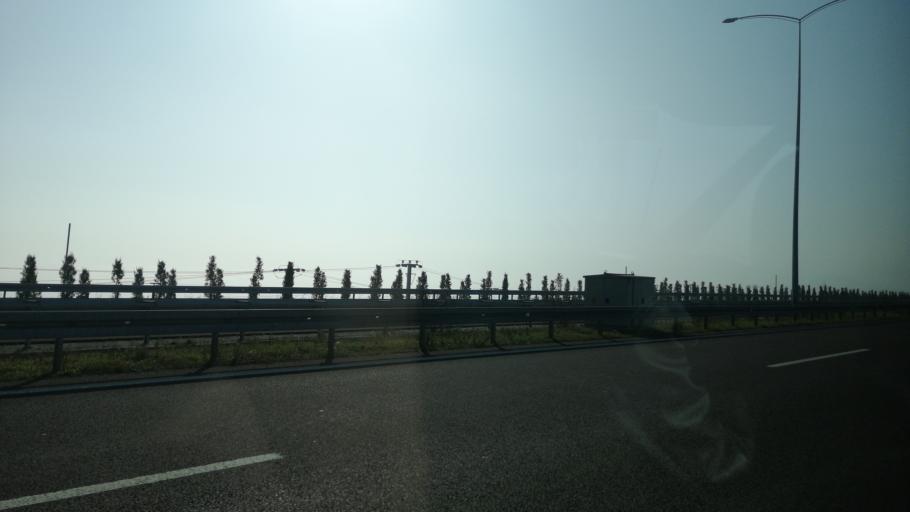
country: TR
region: Yalova
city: Altinova
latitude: 40.7220
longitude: 29.5026
